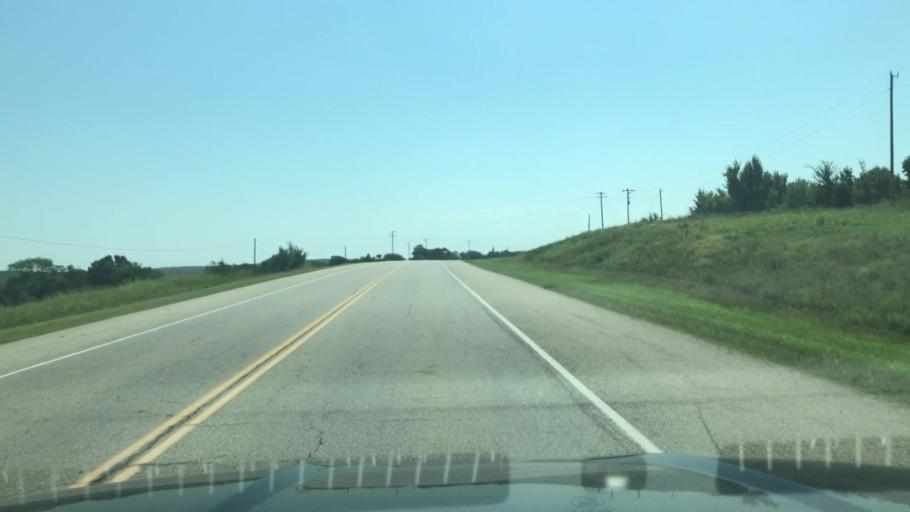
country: US
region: Oklahoma
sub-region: Creek County
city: Kellyville
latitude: 35.9885
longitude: -96.3384
